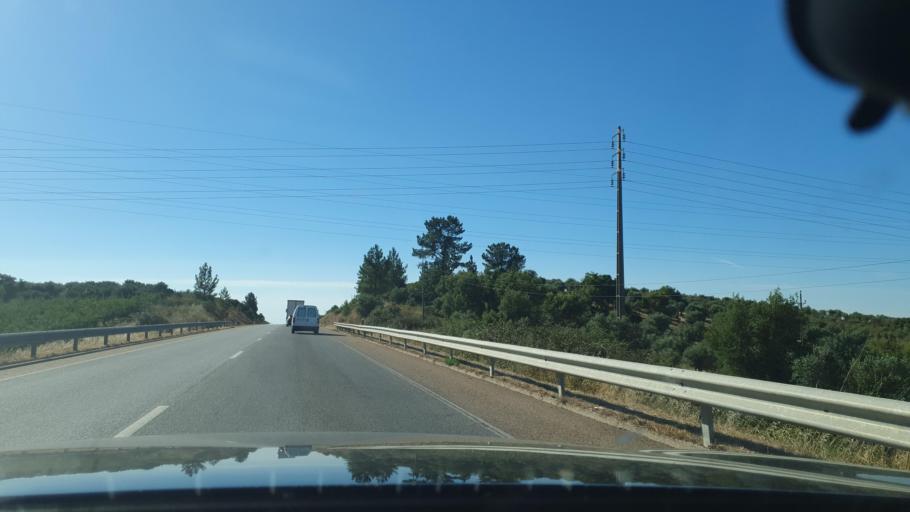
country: PT
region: Evora
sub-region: Borba
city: Borba
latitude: 38.7942
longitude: -7.4637
